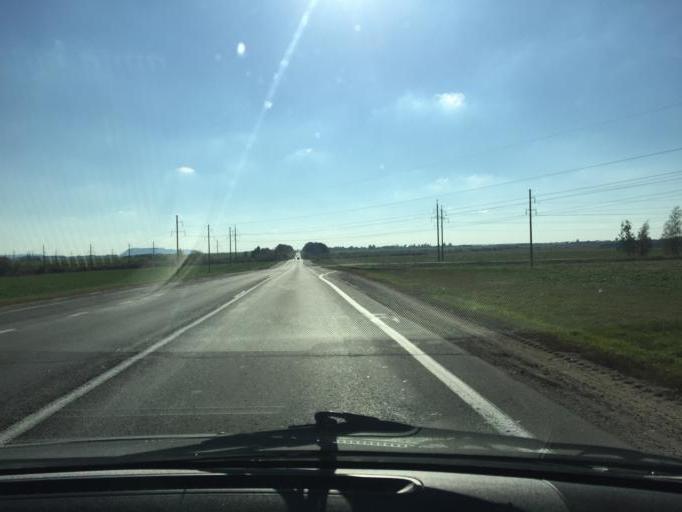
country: BY
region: Minsk
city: Slutsk
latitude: 52.9810
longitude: 27.5041
